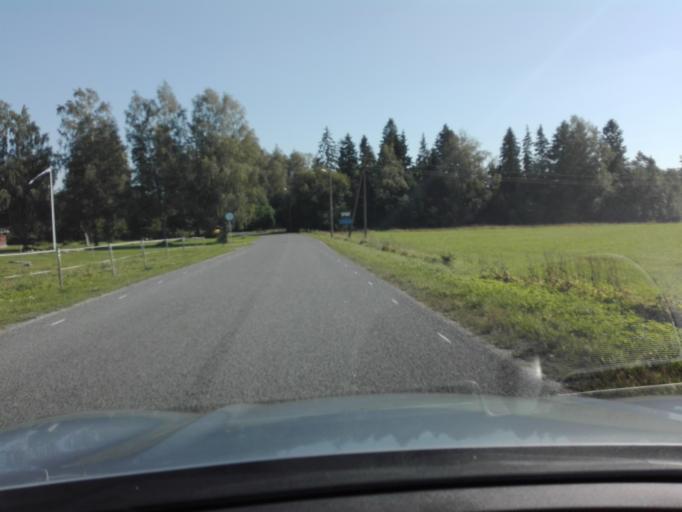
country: EE
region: Raplamaa
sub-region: Rapla vald
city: Rapla
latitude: 59.0661
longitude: 24.8007
